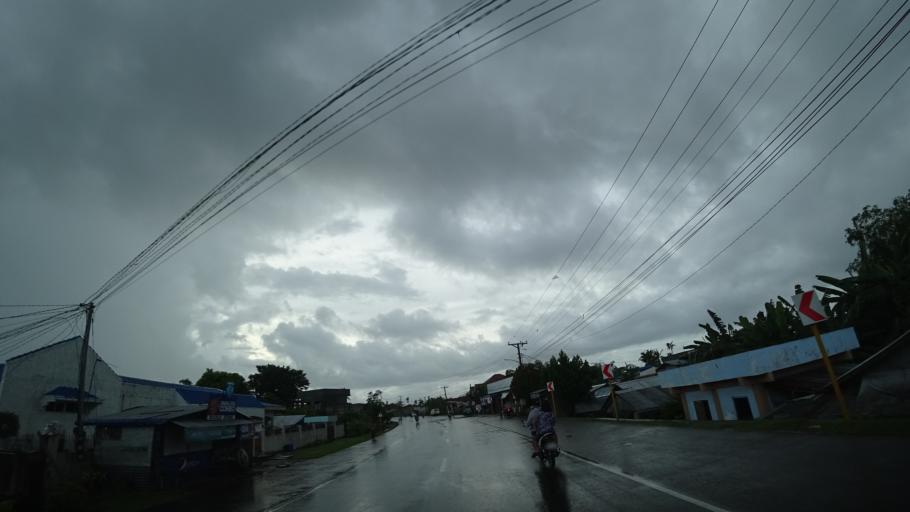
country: PH
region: Eastern Visayas
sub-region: Province of Leyte
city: Tanauan
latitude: 11.1219
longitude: 125.0156
